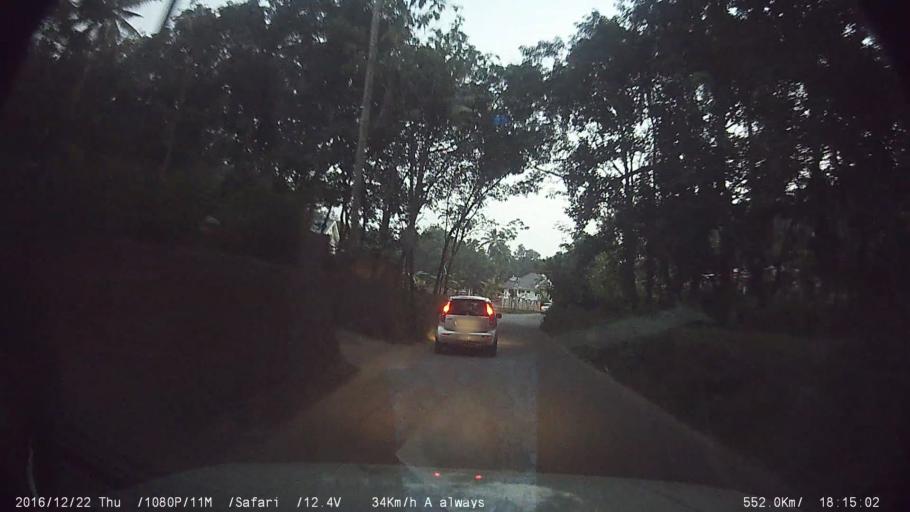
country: IN
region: Kerala
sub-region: Kottayam
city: Palackattumala
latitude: 9.7754
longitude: 76.6128
